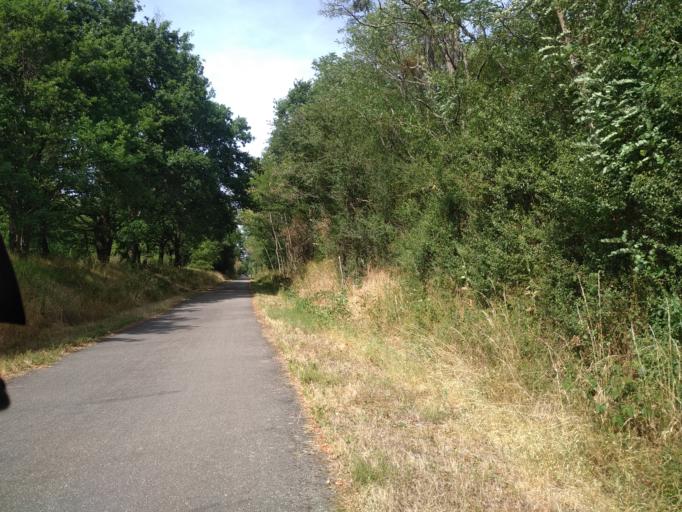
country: FR
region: Auvergne
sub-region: Departement de l'Allier
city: Diou
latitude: 46.5546
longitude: 3.7438
